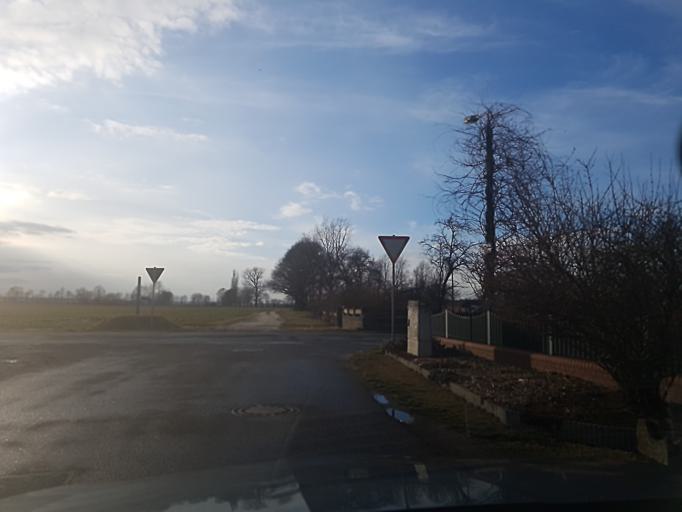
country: DE
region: Brandenburg
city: Schonewalde
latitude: 51.6573
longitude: 13.5902
